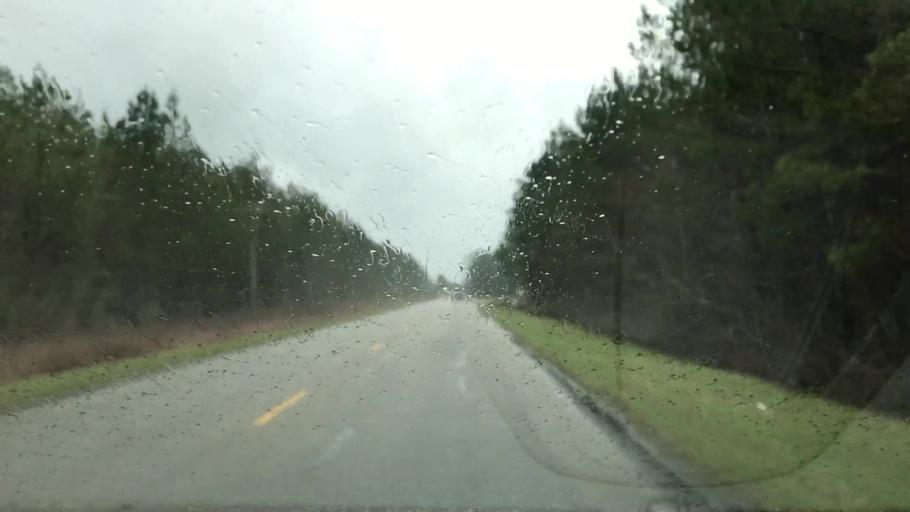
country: US
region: South Carolina
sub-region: Williamsburg County
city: Andrews
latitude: 33.5428
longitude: -79.4760
